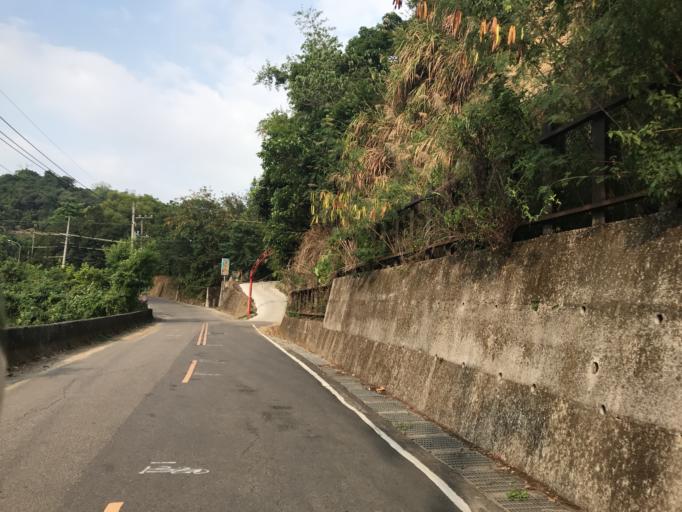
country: TW
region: Taiwan
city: Zhongxing New Village
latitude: 24.0369
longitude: 120.7124
